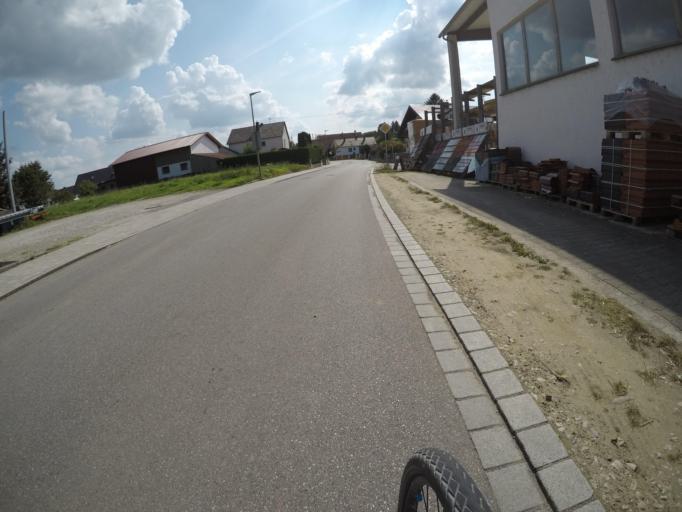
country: DE
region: Bavaria
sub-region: Swabia
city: Westendorf
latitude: 48.5712
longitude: 10.8373
